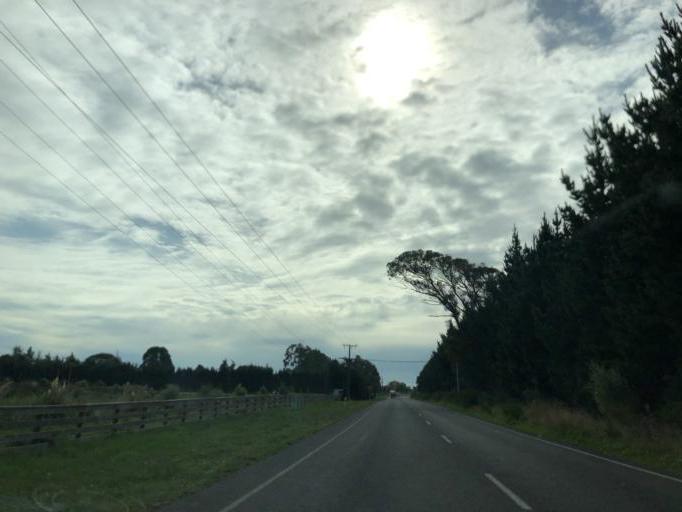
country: NZ
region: Canterbury
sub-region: Selwyn District
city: Rolleston
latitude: -43.6241
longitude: 172.4101
